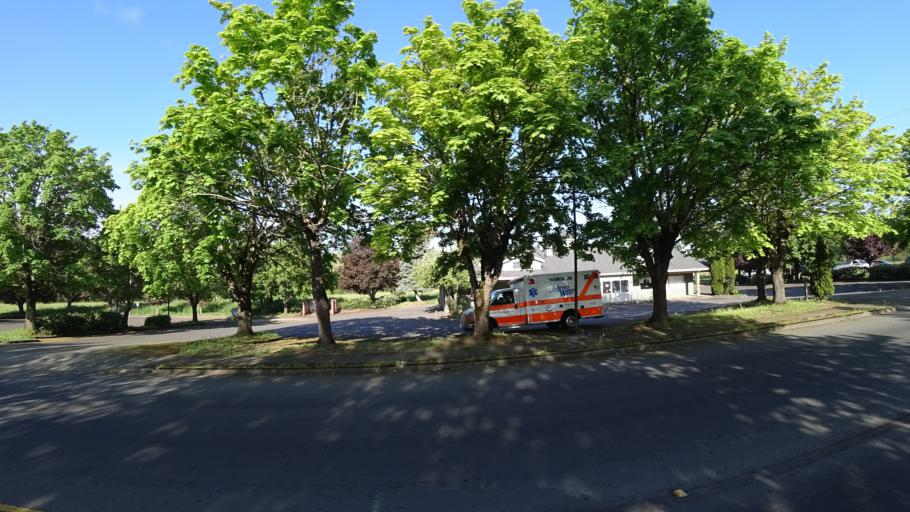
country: US
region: Oregon
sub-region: Washington County
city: Hillsboro
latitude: 45.5193
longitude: -123.0076
